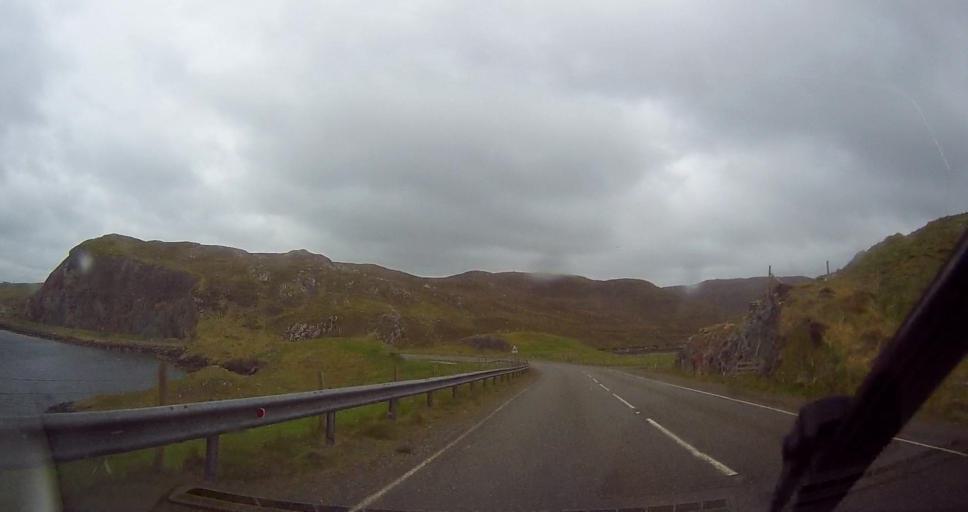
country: GB
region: Scotland
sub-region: Shetland Islands
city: Lerwick
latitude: 60.4002
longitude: -1.3837
